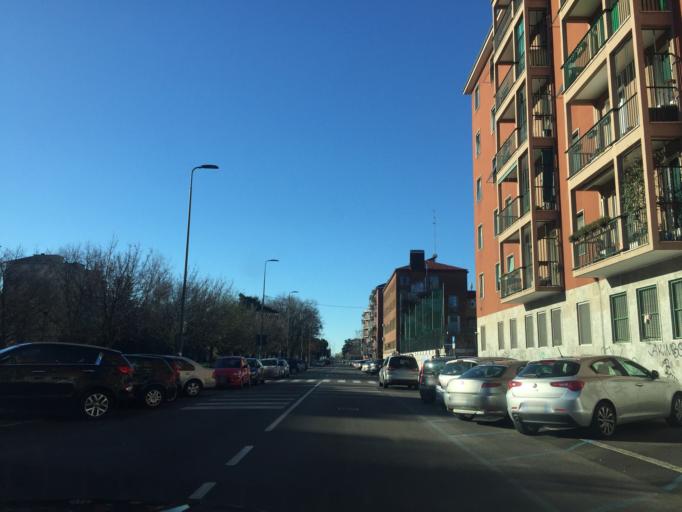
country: IT
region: Lombardy
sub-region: Citta metropolitana di Milano
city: Milano
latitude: 45.4407
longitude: 9.1851
